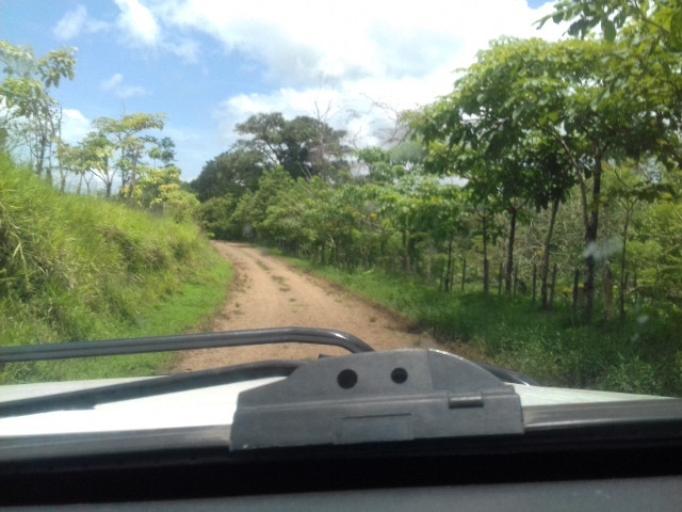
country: NI
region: Matagalpa
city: Matiguas
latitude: 13.0156
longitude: -85.4023
